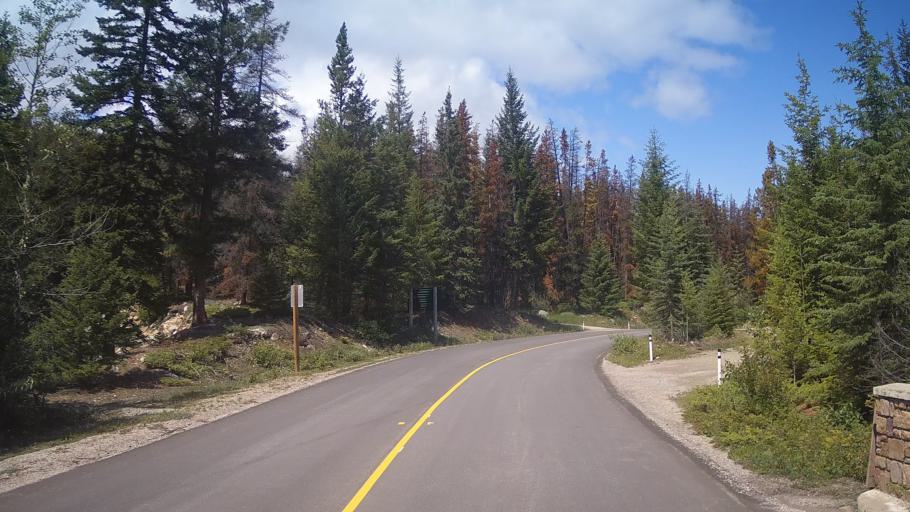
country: CA
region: Alberta
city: Jasper Park Lodge
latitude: 52.7743
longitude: -118.0321
